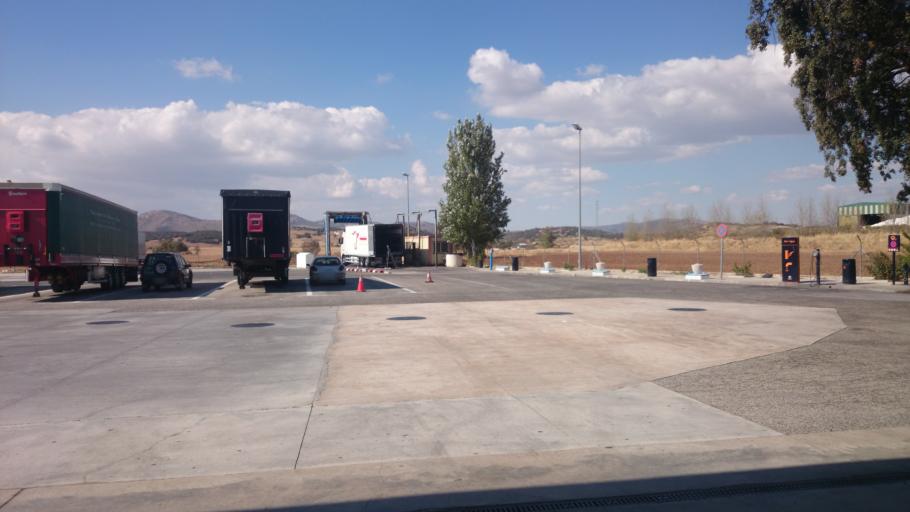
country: ES
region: Andalusia
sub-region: Provincia de Malaga
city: Villanueva del Trabuco
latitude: 37.0693
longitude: -4.3286
